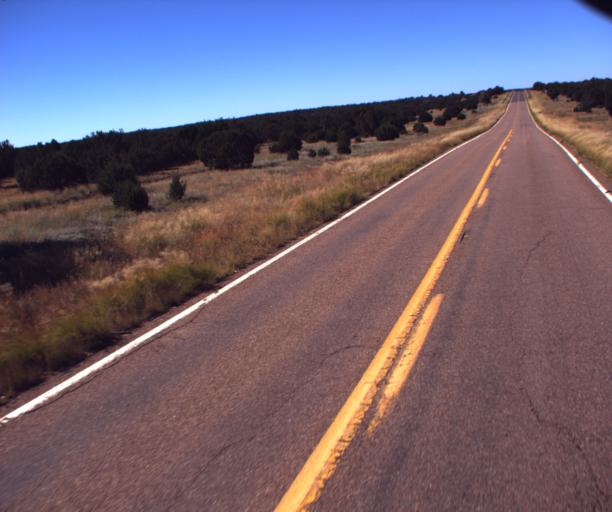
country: US
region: Arizona
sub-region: Navajo County
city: Heber-Overgaard
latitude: 34.4572
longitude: -110.4410
